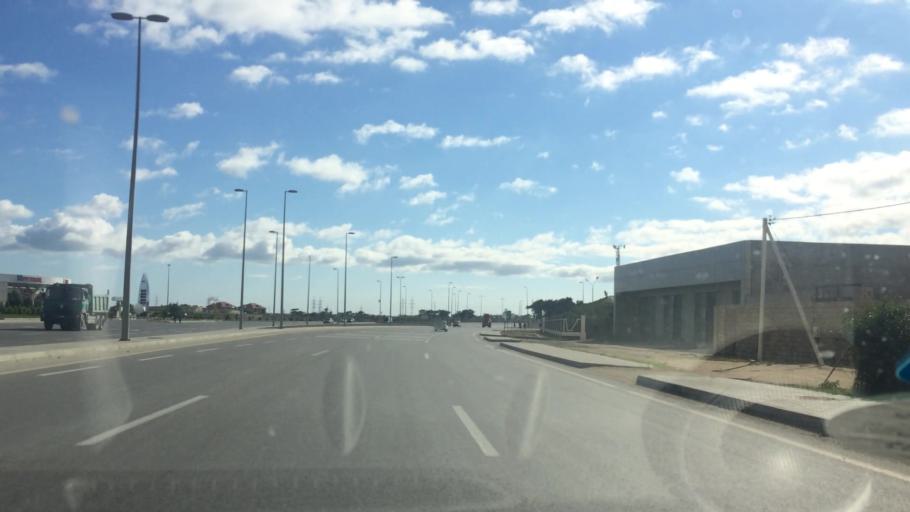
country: AZ
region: Baki
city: Qala
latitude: 40.4451
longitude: 50.1744
